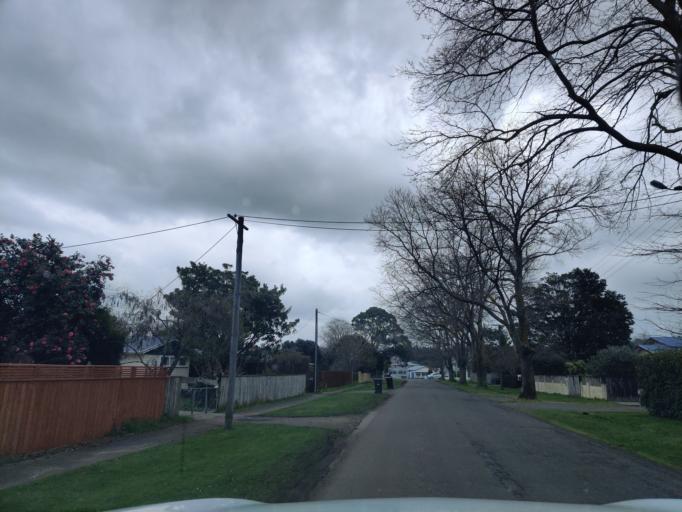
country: NZ
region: Manawatu-Wanganui
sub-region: Palmerston North City
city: Palmerston North
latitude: -40.2872
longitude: 175.7549
